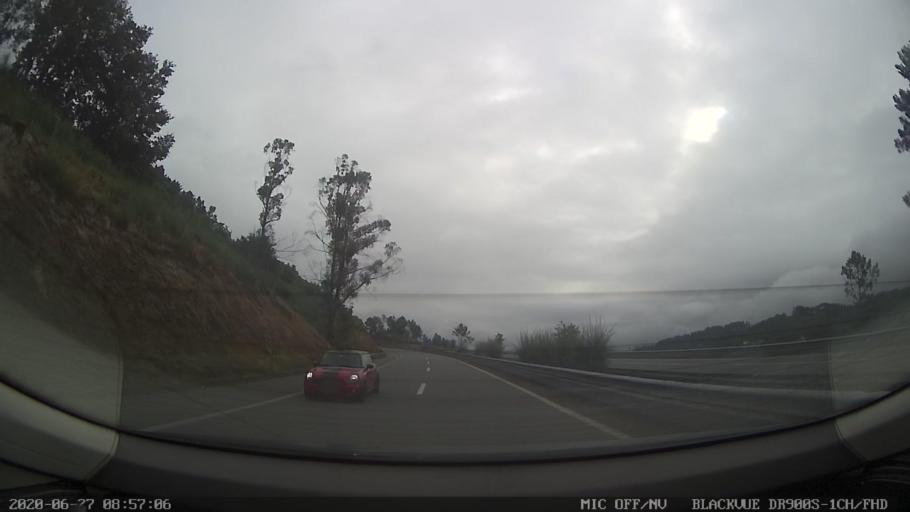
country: PT
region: Porto
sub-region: Amarante
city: Amarante
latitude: 41.2469
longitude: -8.1112
